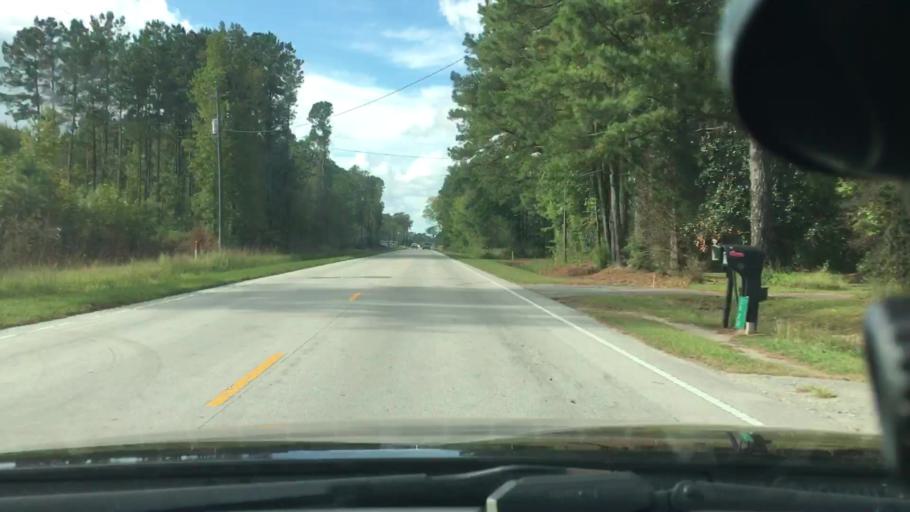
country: US
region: North Carolina
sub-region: Craven County
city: Vanceboro
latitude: 35.3463
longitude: -77.1832
